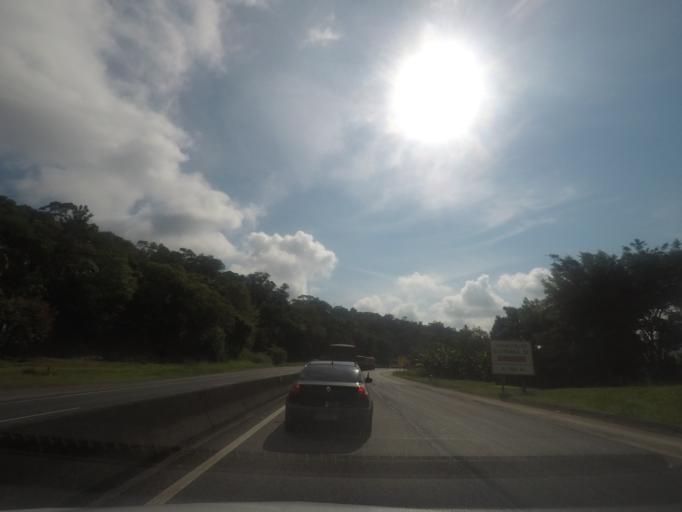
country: BR
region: Parana
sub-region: Antonina
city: Antonina
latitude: -25.5699
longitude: -48.8143
